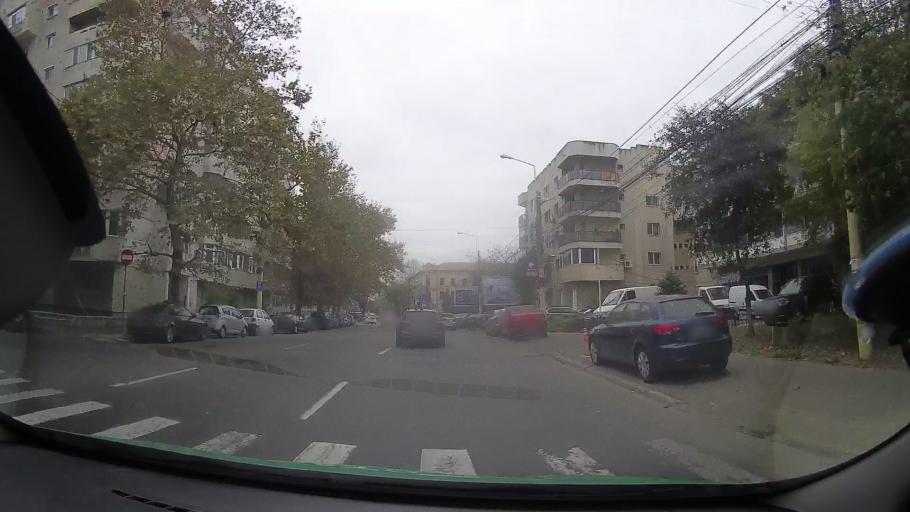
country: RO
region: Constanta
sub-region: Municipiul Constanta
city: Constanta
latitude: 44.1802
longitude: 28.6526
